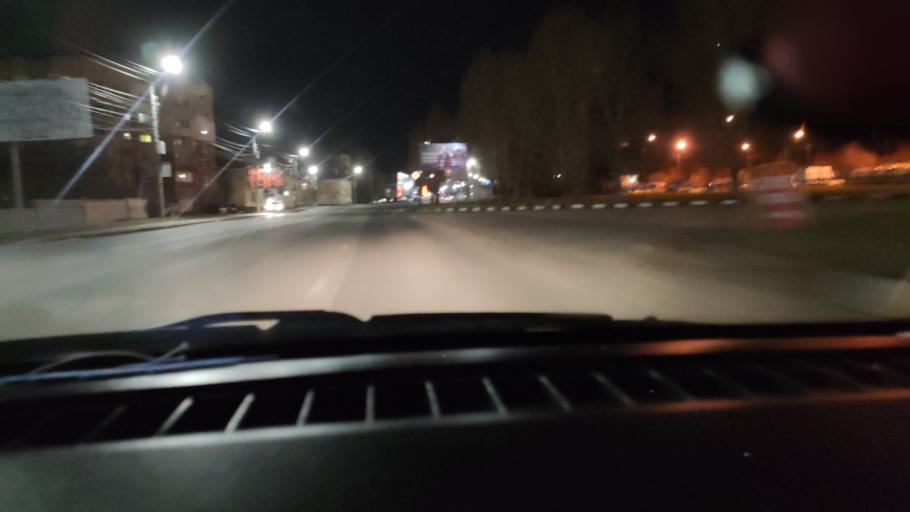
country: RU
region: Saratov
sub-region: Saratovskiy Rayon
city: Saratov
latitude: 51.5577
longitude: 46.0547
